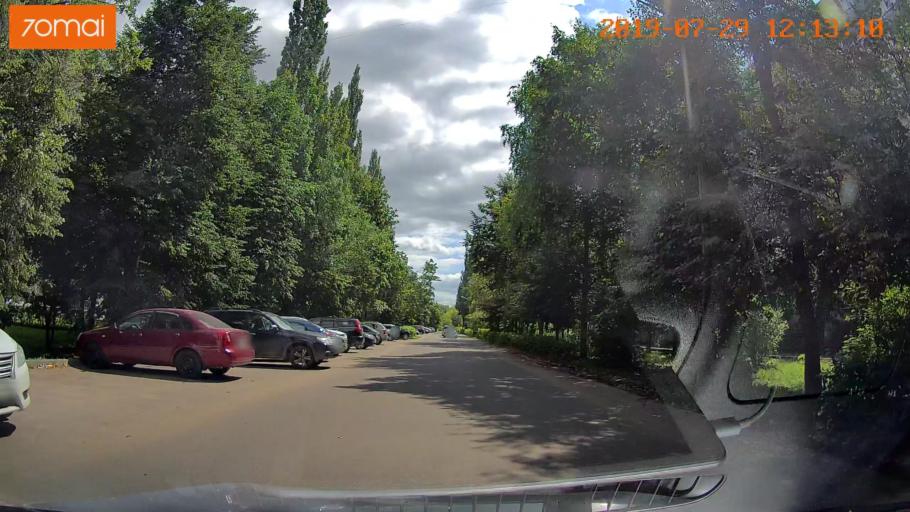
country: RU
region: Moskovskaya
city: Voskresensk
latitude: 55.3147
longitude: 38.6508
